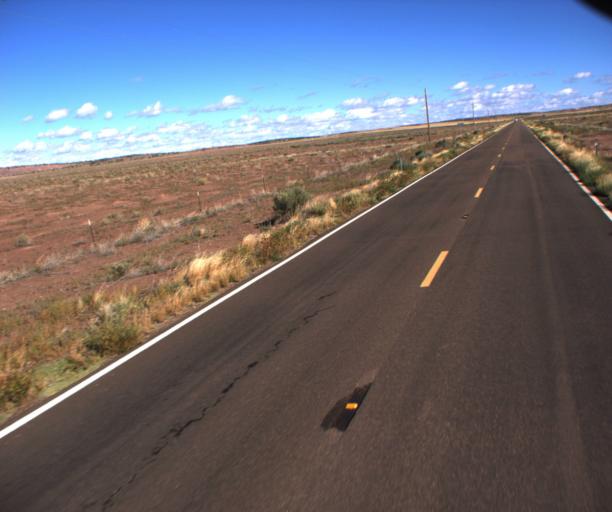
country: US
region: Arizona
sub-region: Apache County
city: Saint Johns
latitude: 34.6202
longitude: -109.3161
